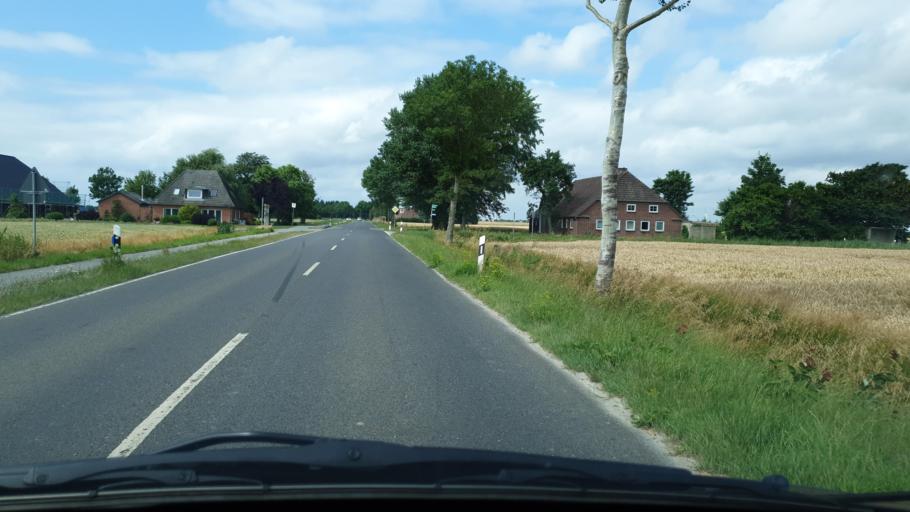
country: DE
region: Schleswig-Holstein
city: Friedrichskoog
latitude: 53.9828
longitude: 8.9155
